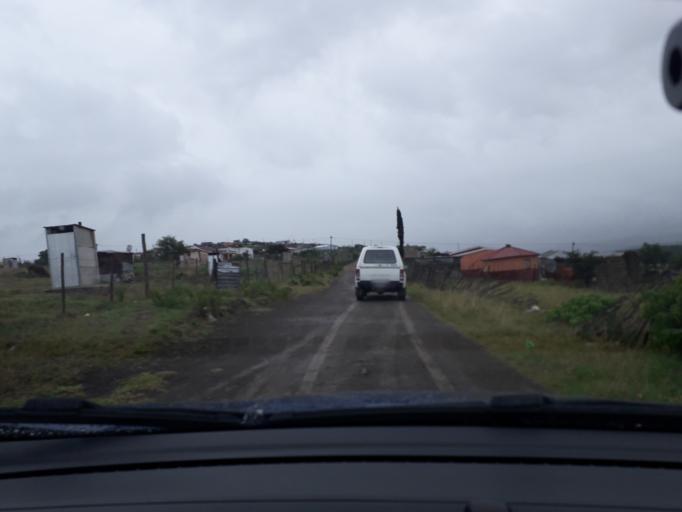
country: ZA
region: Eastern Cape
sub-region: Buffalo City Metropolitan Municipality
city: Bhisho
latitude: -32.8082
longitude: 27.3659
